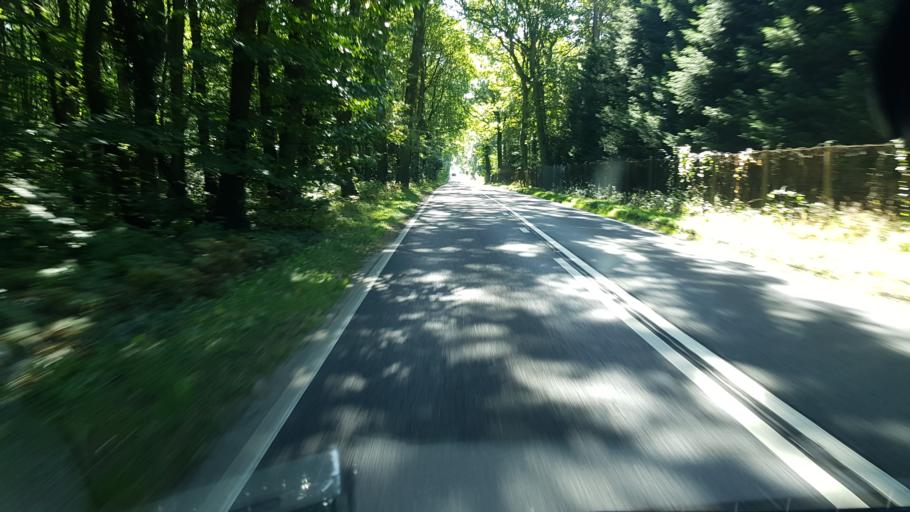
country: GB
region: England
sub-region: Kent
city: Kings Hill
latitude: 51.2742
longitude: 0.3559
